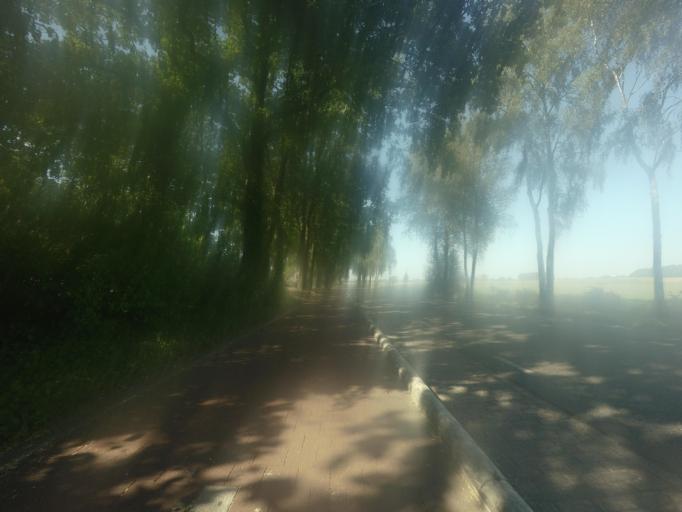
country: NL
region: North Brabant
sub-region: Gemeente Goirle
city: Goirle
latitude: 51.5123
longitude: 5.0868
